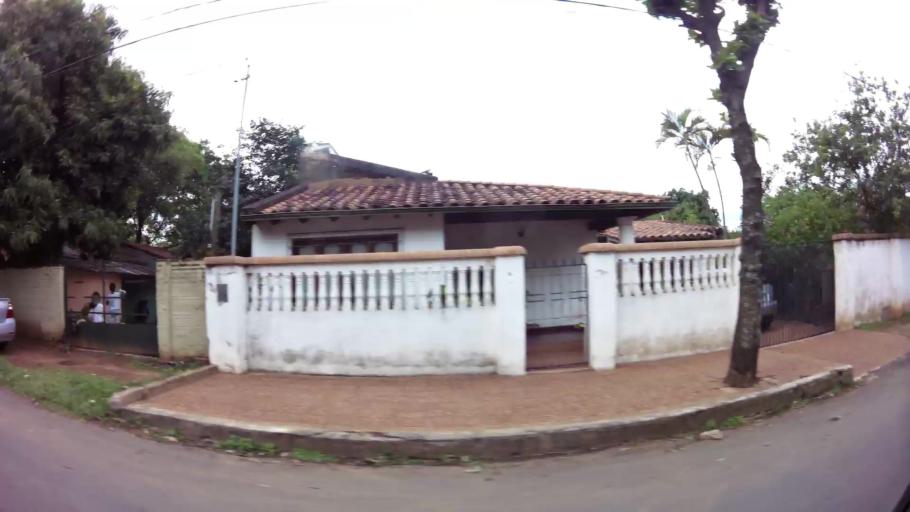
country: PY
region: Central
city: San Lorenzo
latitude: -25.2747
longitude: -57.4868
